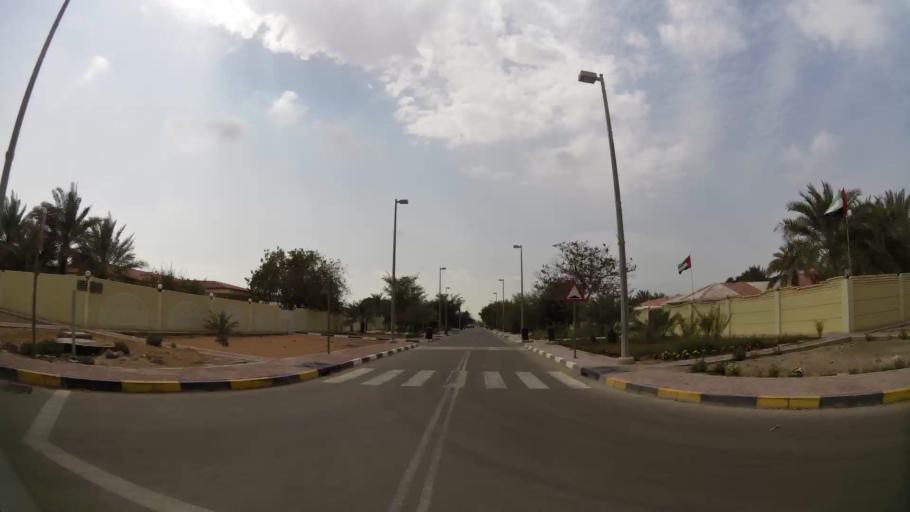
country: AE
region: Abu Dhabi
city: Abu Dhabi
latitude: 24.5223
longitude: 54.6784
